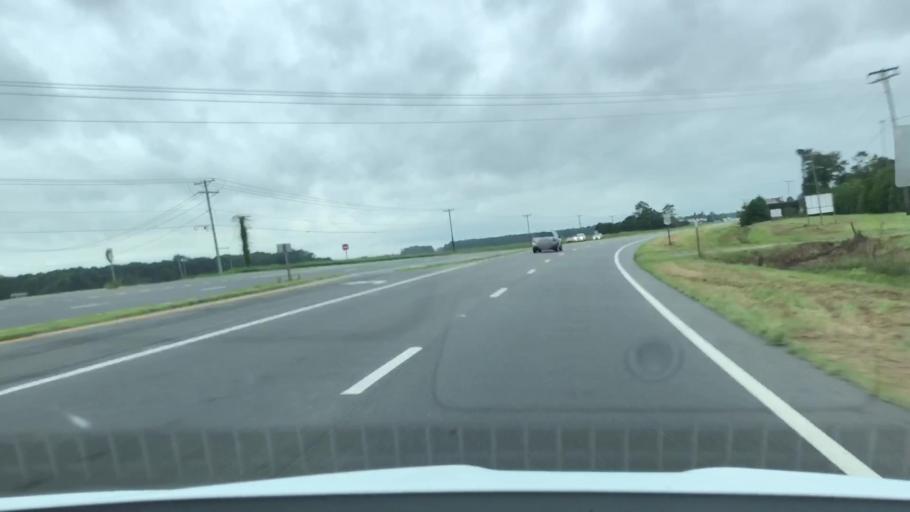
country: US
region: North Carolina
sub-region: Lenoir County
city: La Grange
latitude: 35.2604
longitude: -77.7129
